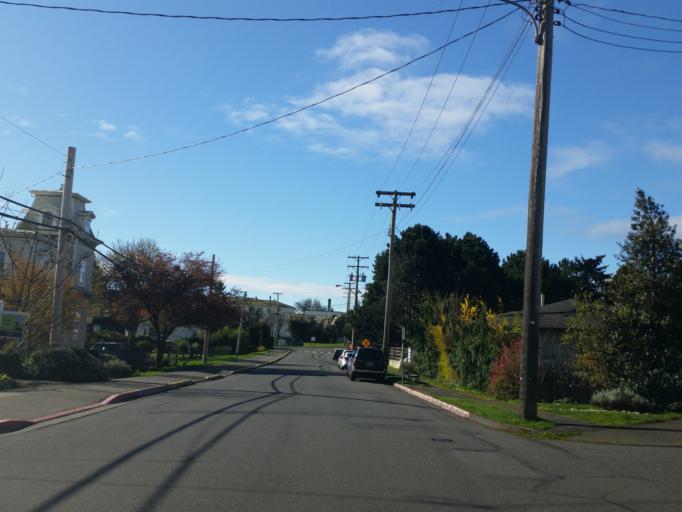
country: CA
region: British Columbia
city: Victoria
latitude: 48.4282
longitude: -123.3991
